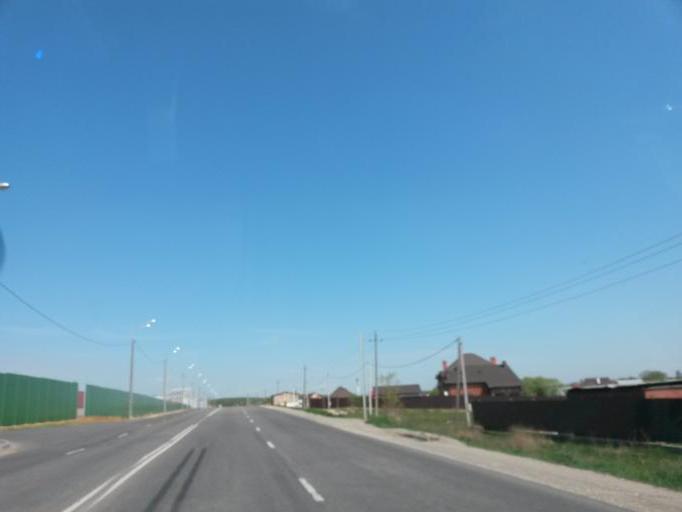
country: RU
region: Moskovskaya
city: Klimovsk
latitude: 55.3357
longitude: 37.5993
